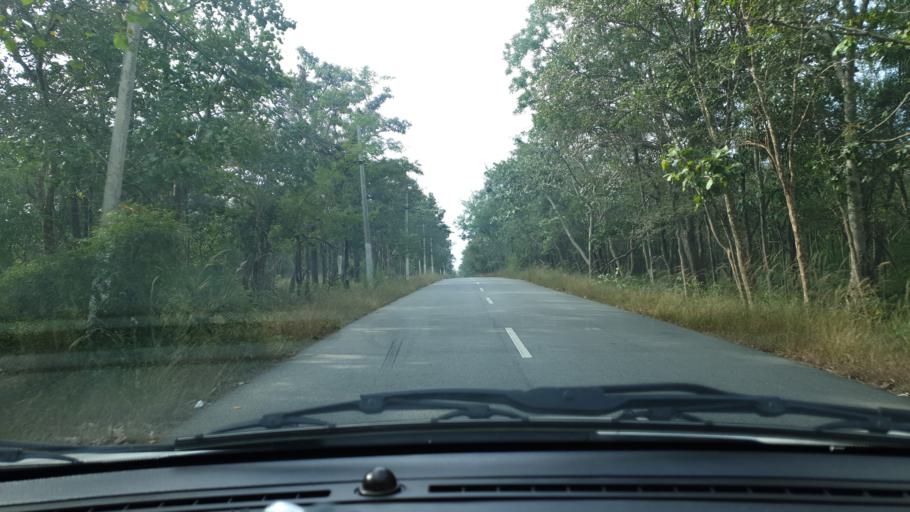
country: IN
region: Andhra Pradesh
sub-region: Kurnool
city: Srisailam
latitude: 16.2882
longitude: 78.7290
